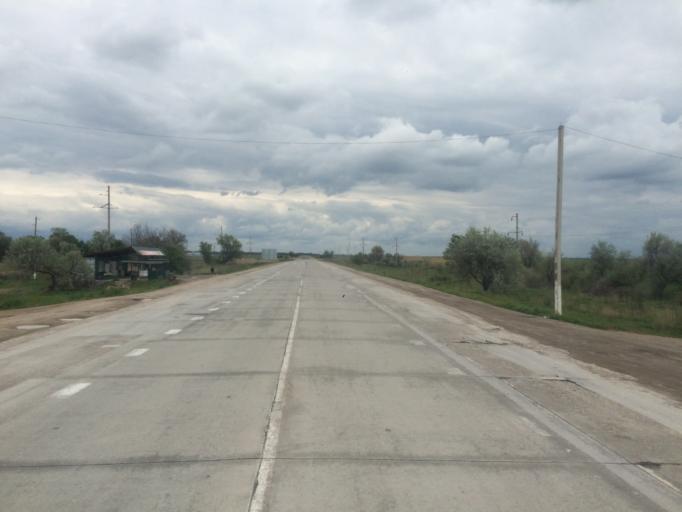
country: KG
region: Chuy
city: Sokuluk
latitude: 43.2712
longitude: 74.2403
